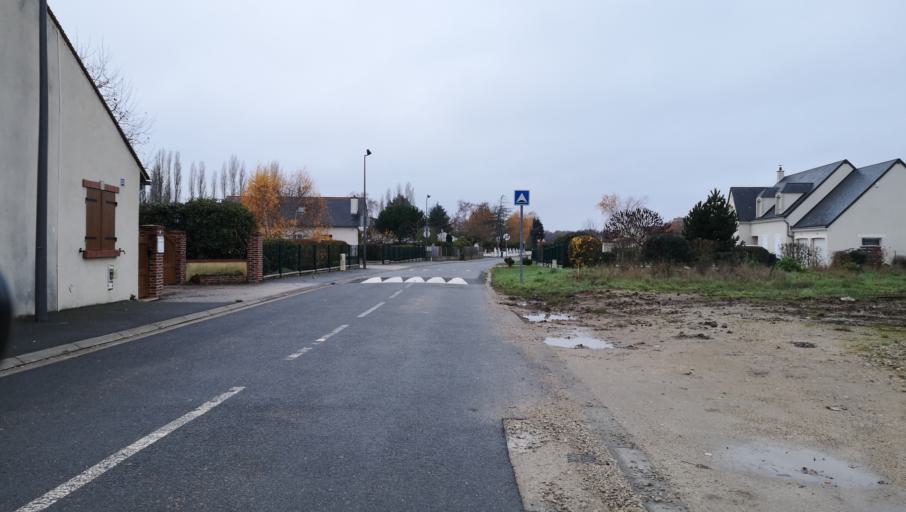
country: FR
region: Centre
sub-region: Departement du Loiret
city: Marigny-les-Usages
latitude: 47.9528
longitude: 2.0141
